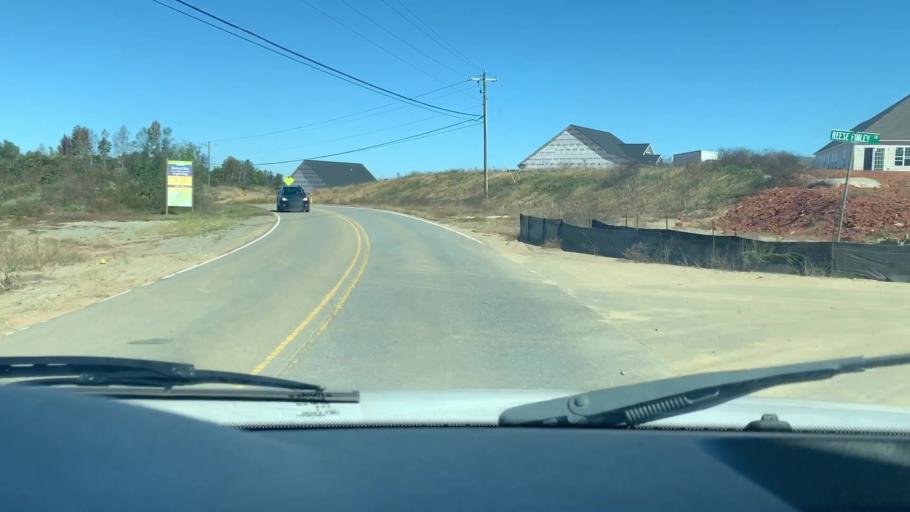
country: US
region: North Carolina
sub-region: Gaston County
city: Davidson
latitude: 35.4643
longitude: -80.8216
